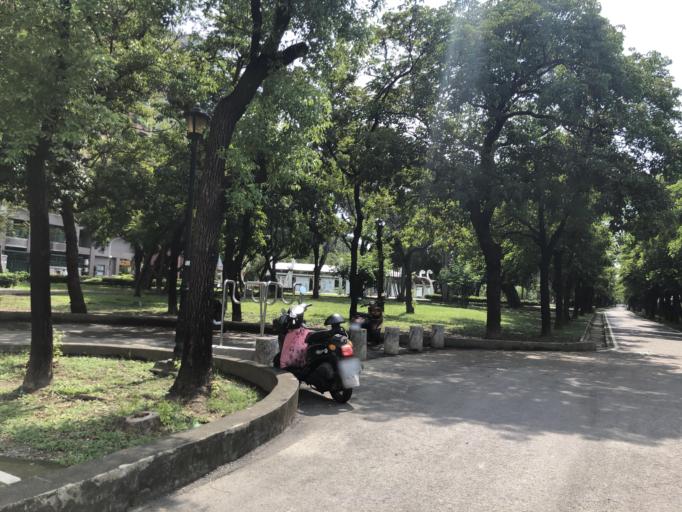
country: TW
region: Kaohsiung
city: Kaohsiung
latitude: 22.6821
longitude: 120.3024
